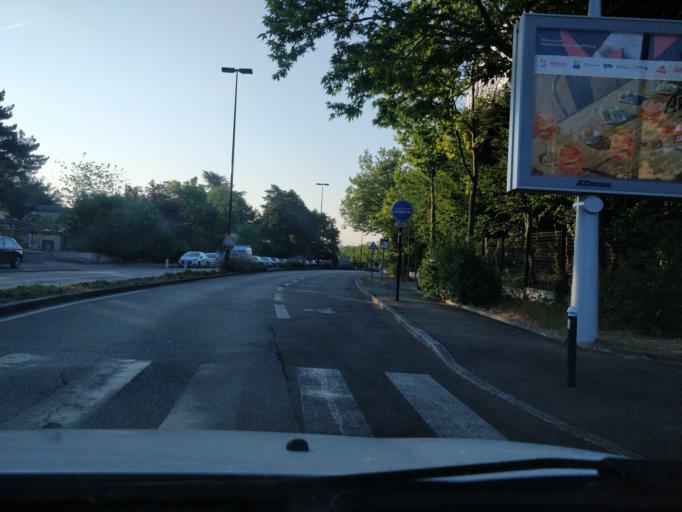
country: FR
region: Pays de la Loire
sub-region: Departement de la Loire-Atlantique
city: La Chapelle-sur-Erdre
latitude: 47.2606
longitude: -1.5616
